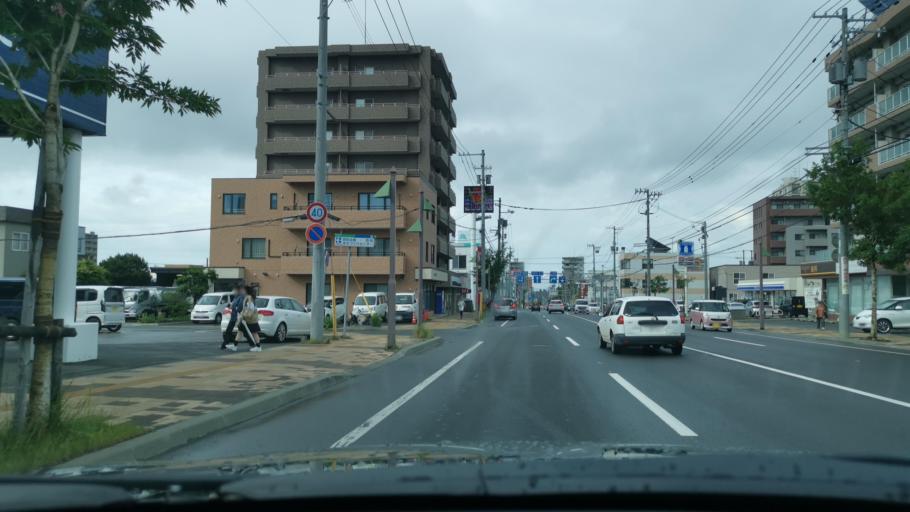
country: JP
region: Hokkaido
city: Sapporo
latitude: 43.0784
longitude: 141.2866
